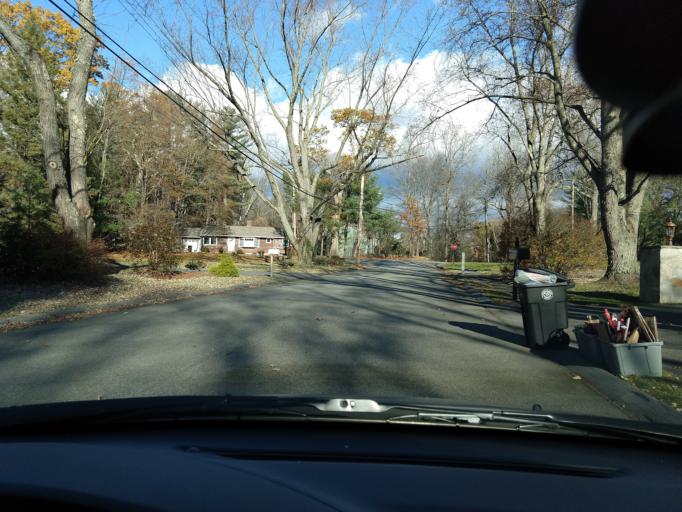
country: US
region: Massachusetts
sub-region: Middlesex County
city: Bedford
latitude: 42.4957
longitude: -71.2491
